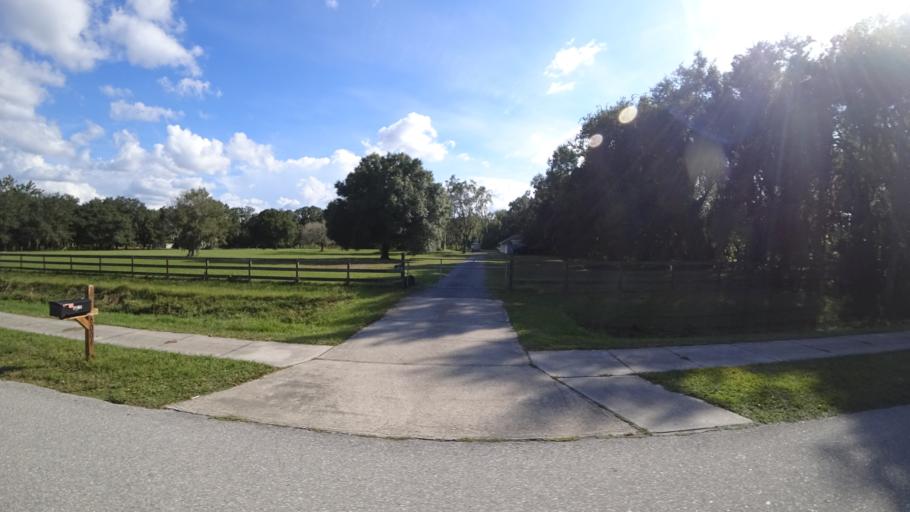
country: US
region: Florida
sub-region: Manatee County
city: Samoset
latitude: 27.4708
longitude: -82.4849
